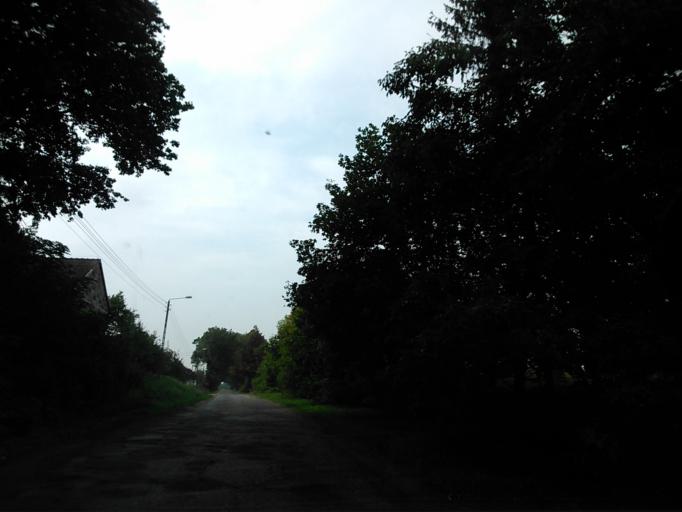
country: PL
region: Kujawsko-Pomorskie
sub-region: Powiat wabrzeski
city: Pluznica
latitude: 53.2354
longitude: 18.8220
